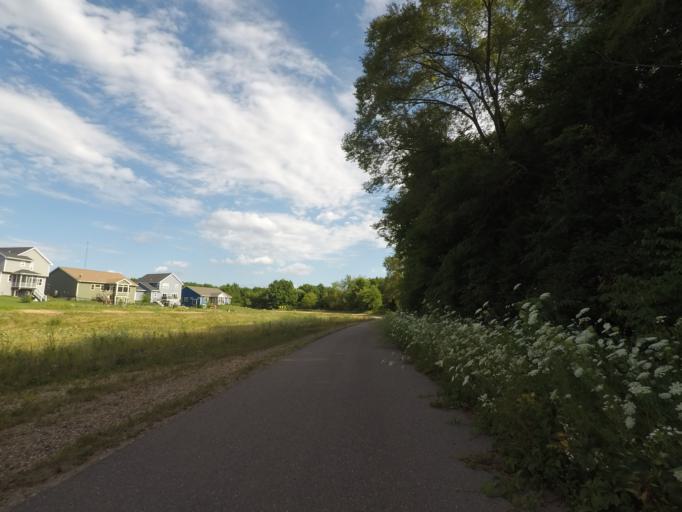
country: US
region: Wisconsin
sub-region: Dane County
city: Middleton
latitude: 43.0687
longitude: -89.5613
